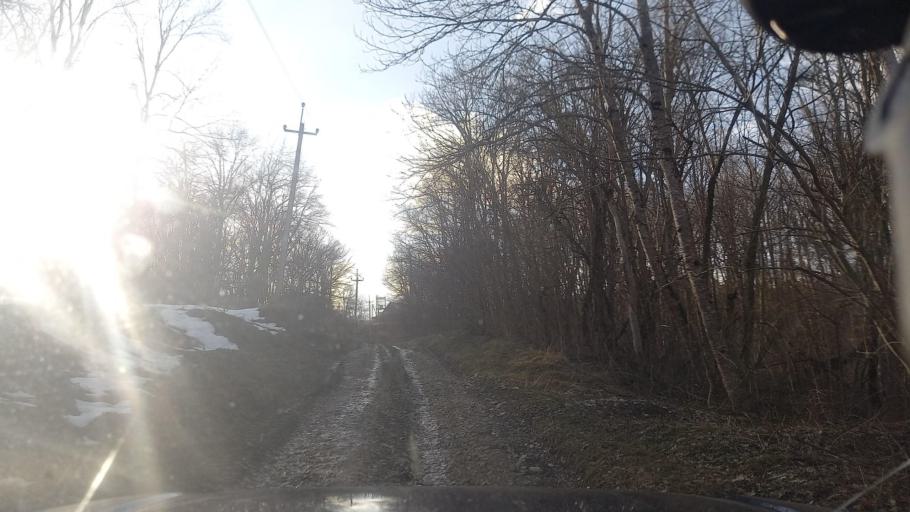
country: RU
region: Krasnodarskiy
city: Goryachiy Klyuch
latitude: 44.6882
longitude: 38.9846
